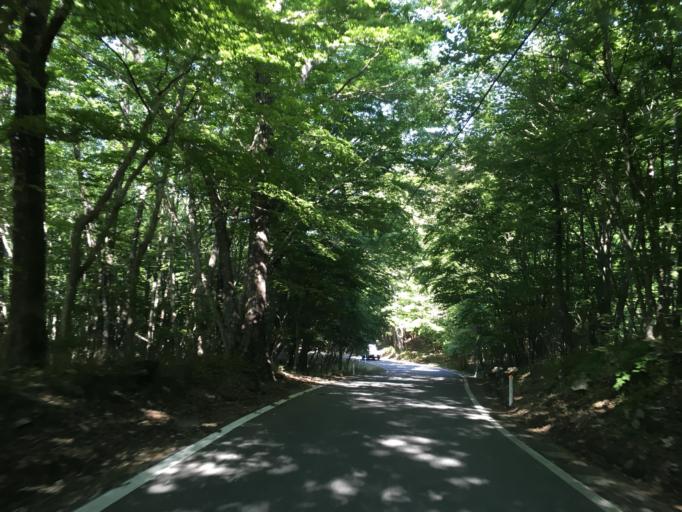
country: JP
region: Iwate
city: Kamaishi
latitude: 39.1962
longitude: 141.8233
